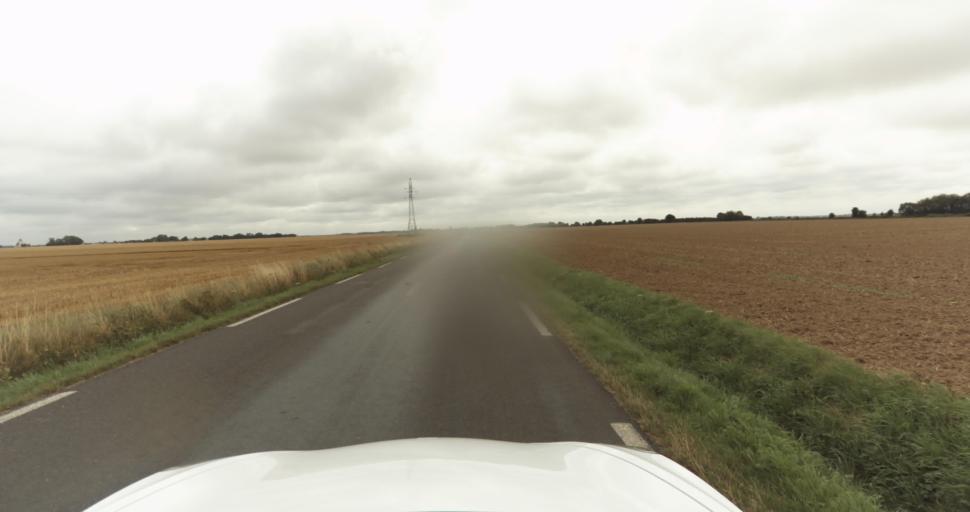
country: FR
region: Haute-Normandie
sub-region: Departement de l'Eure
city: Claville
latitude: 49.0836
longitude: 1.0523
